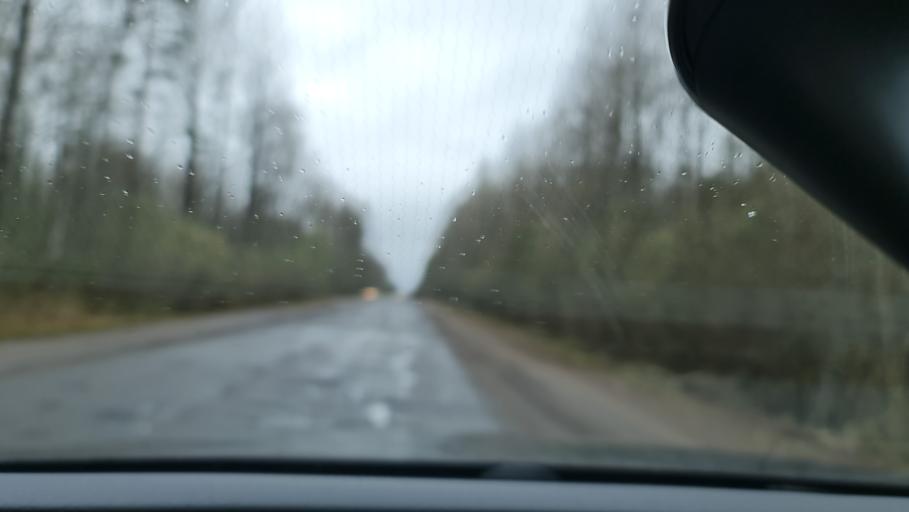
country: RU
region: Novgorod
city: Demyansk
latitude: 57.6742
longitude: 32.5493
